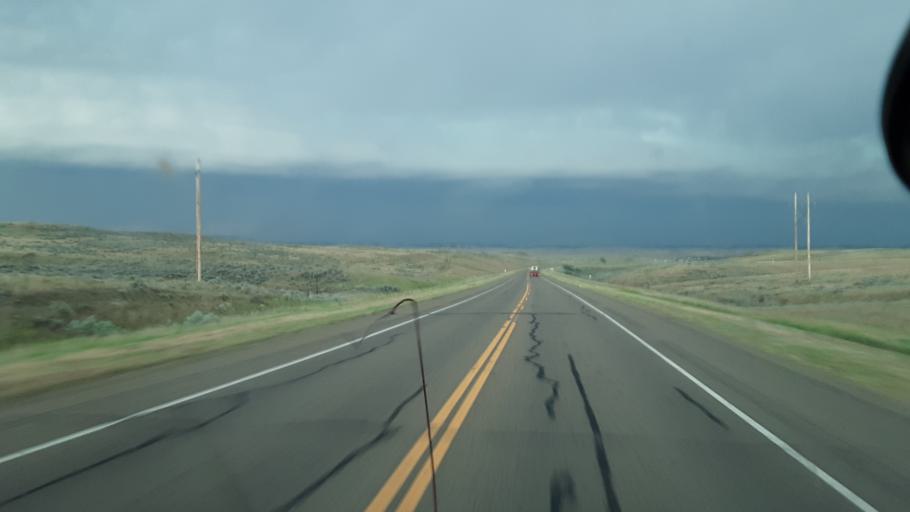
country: US
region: Montana
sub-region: Powder River County
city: Broadus
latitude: 45.4011
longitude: -105.3647
